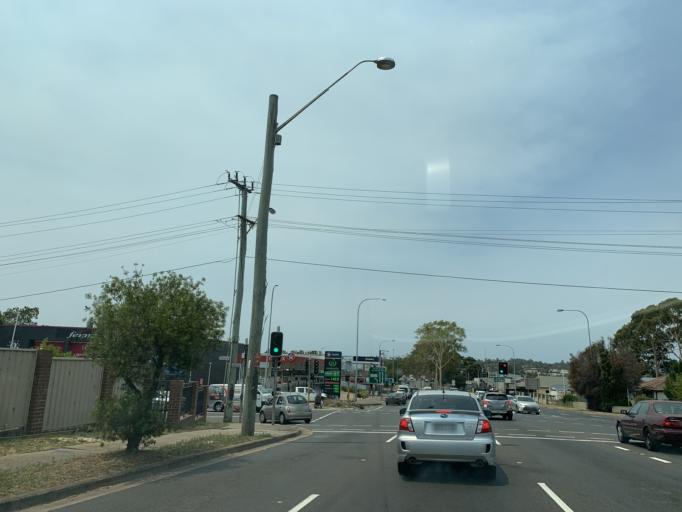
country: AU
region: New South Wales
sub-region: Blacktown
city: Blacktown
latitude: -33.7770
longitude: 150.9329
